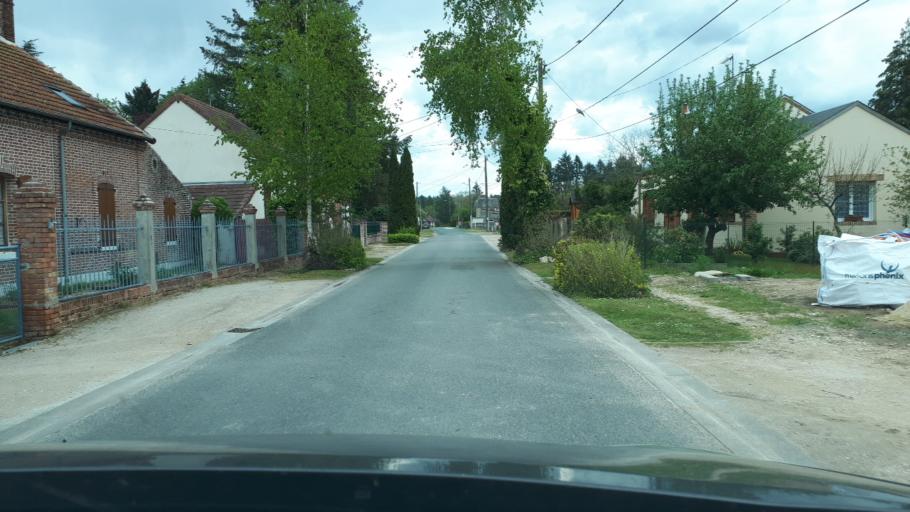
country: FR
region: Centre
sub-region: Departement du Loir-et-Cher
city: Souesmes
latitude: 47.5097
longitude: 2.1541
